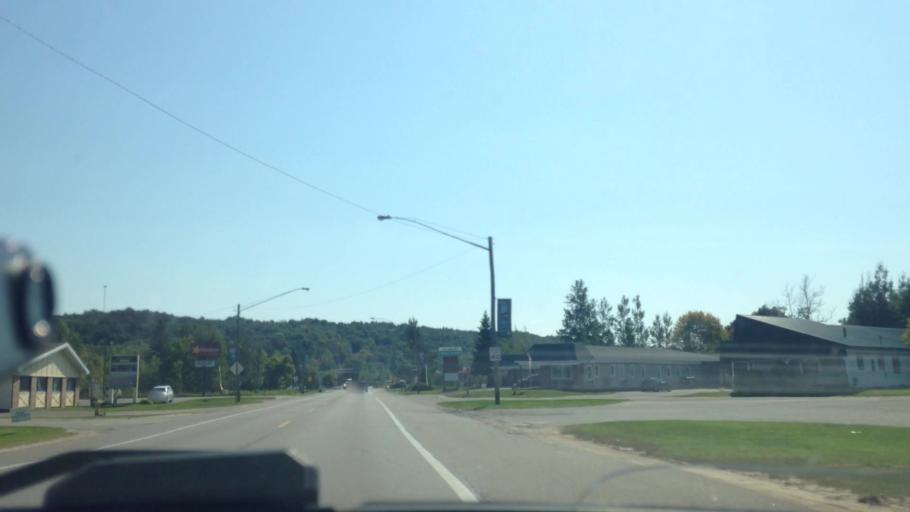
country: US
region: Michigan
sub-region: Alger County
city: Munising
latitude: 46.4063
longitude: -86.6504
